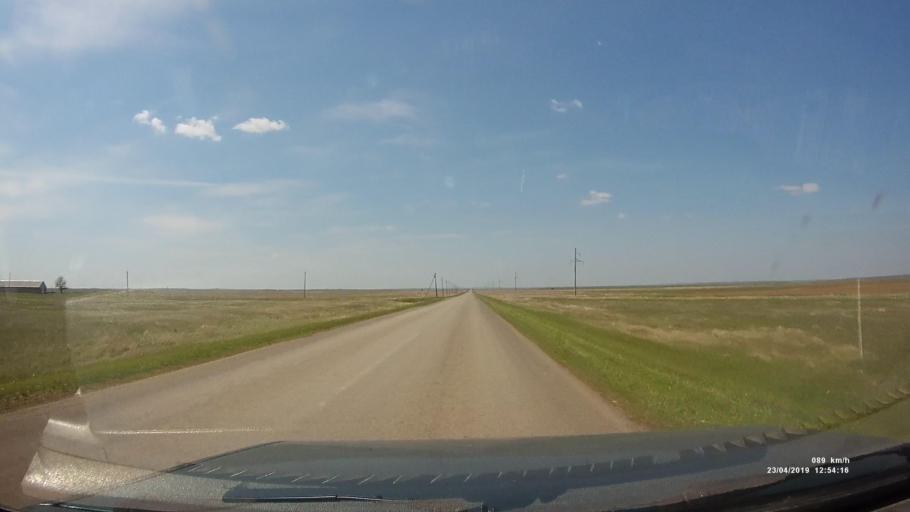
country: RU
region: Kalmykiya
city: Yashalta
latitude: 46.5791
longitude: 42.5809
